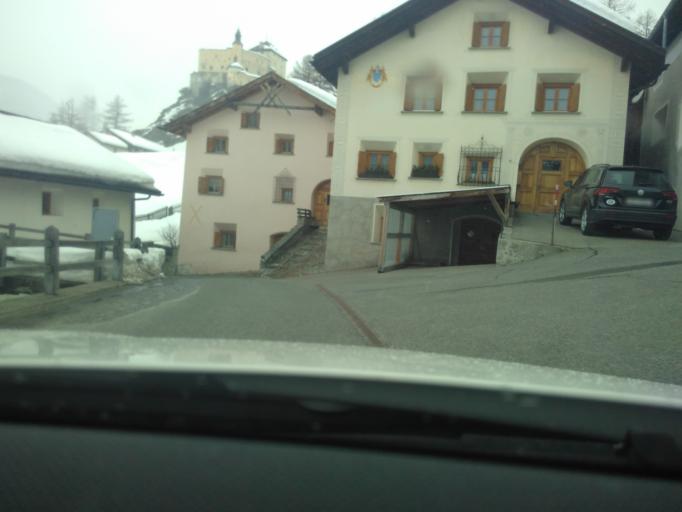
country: CH
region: Grisons
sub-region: Inn District
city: Scuol
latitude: 46.7796
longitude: 10.2647
